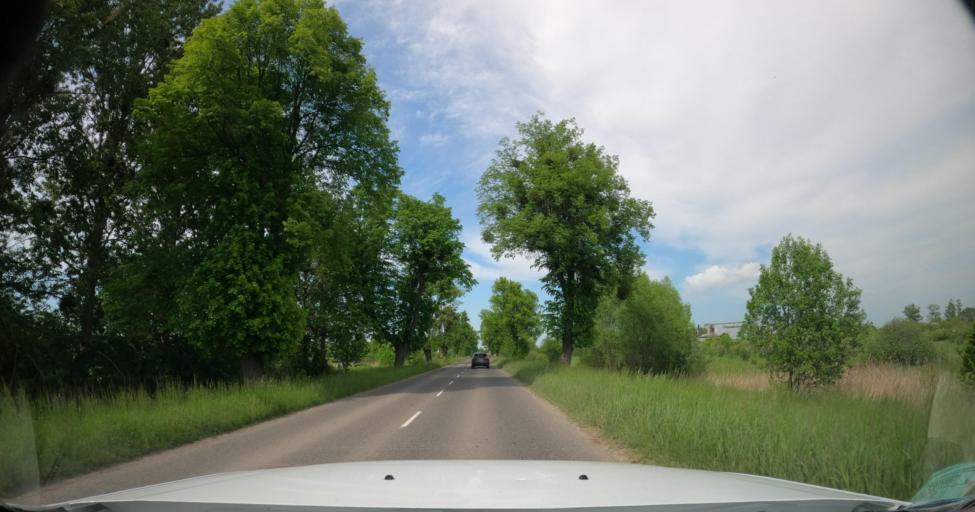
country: PL
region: Warmian-Masurian Voivodeship
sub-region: Powiat lidzbarski
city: Lidzbark Warminski
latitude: 54.1362
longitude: 20.5661
